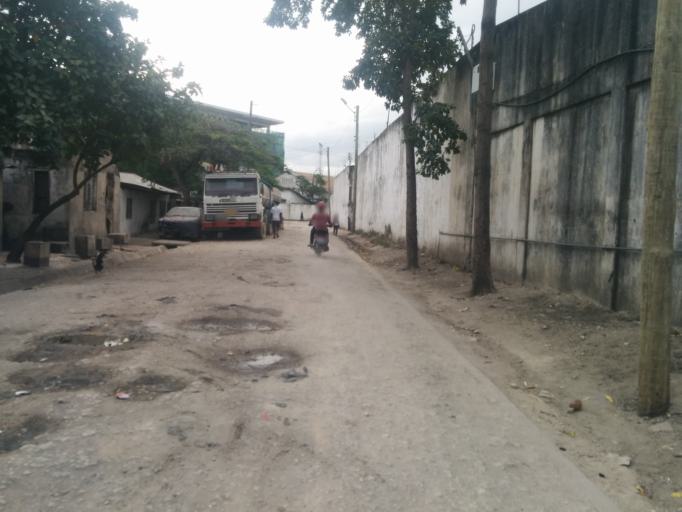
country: TZ
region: Dar es Salaam
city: Dar es Salaam
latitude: -6.8337
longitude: 39.2764
